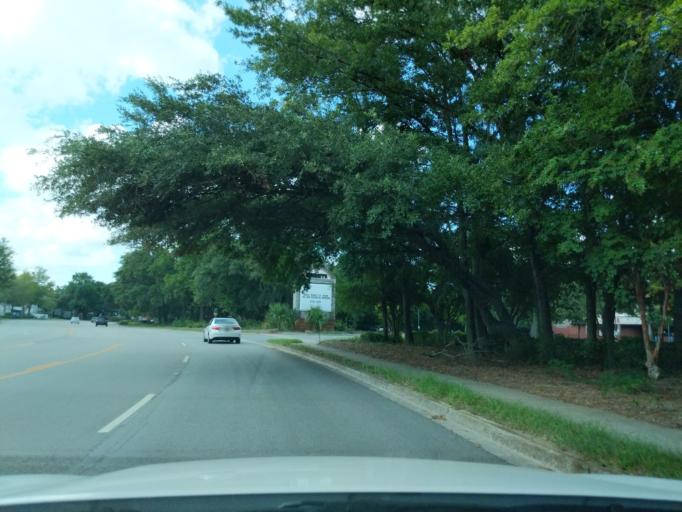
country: US
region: South Carolina
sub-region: Charleston County
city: Mount Pleasant
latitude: 32.7988
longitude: -79.8901
